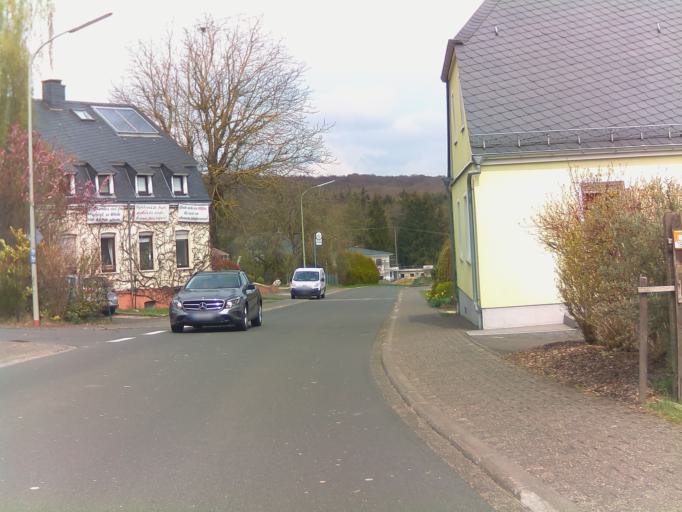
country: DE
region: Rheinland-Pfalz
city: Stipshausen
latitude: 49.8502
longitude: 7.2916
